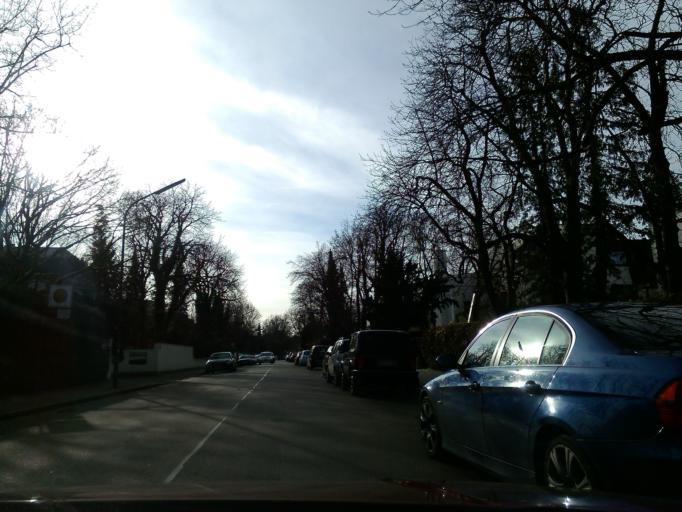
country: DE
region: Bavaria
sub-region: Upper Bavaria
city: Pullach im Isartal
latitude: 48.0835
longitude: 11.5481
